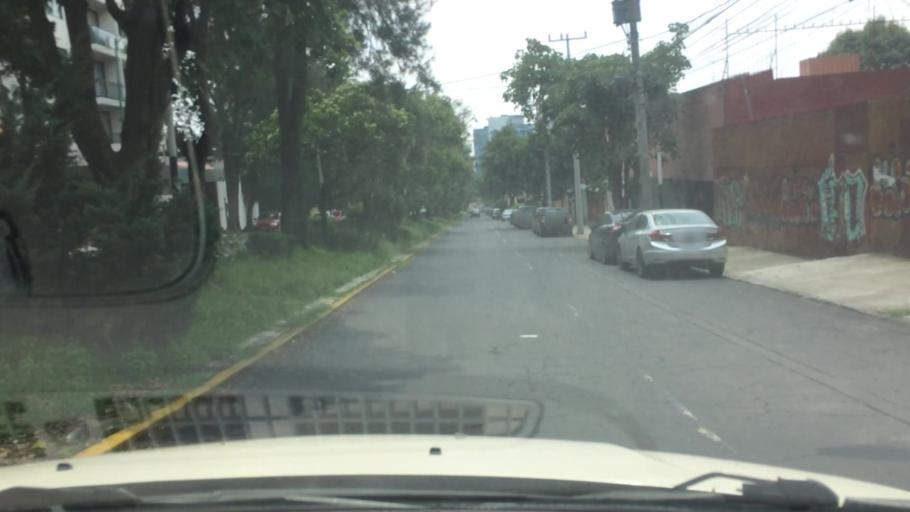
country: MX
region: Mexico City
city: Alvaro Obregon
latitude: 19.3579
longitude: -99.2027
